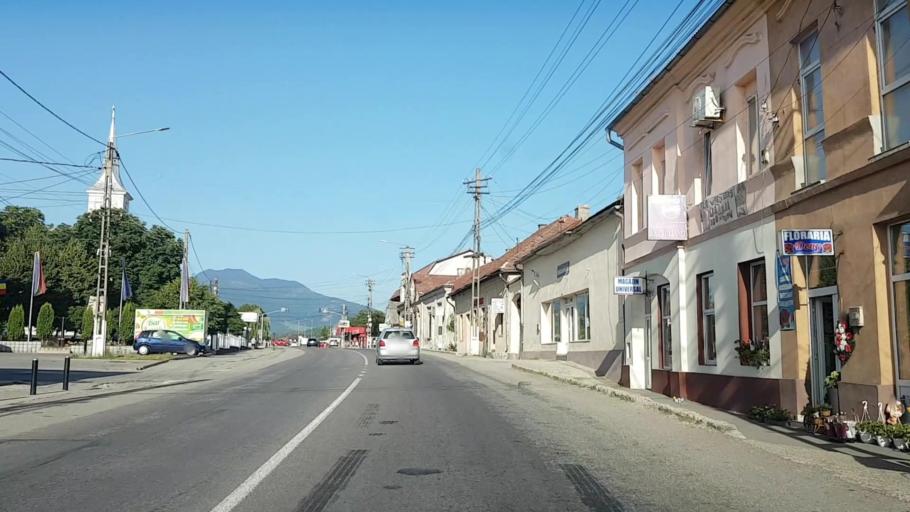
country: RO
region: Bistrita-Nasaud
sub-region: Comuna Bistrita Bargaului
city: Bistrita Bargaului
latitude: 47.2196
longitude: 24.7384
